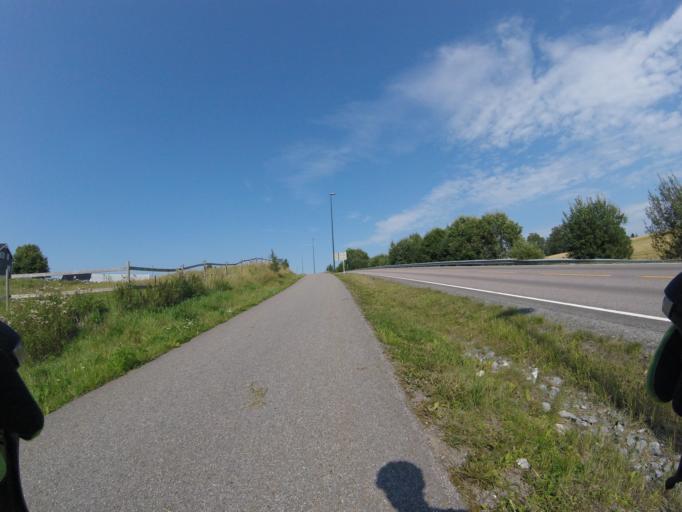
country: NO
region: Akershus
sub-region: Skedsmo
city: Leirsund
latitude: 59.9996
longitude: 11.0993
